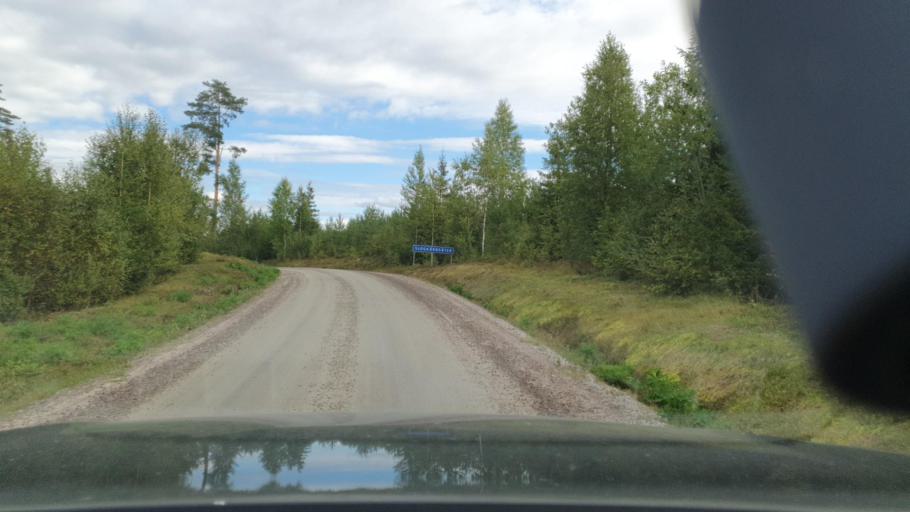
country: SE
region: Vaermland
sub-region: Hagfors Kommun
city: Ekshaerad
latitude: 60.2057
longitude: 13.6315
